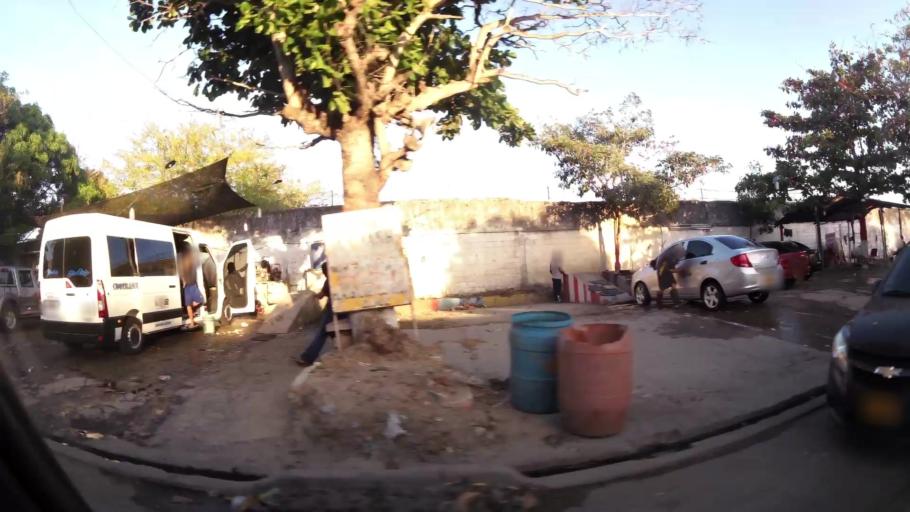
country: CO
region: Atlantico
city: Barranquilla
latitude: 10.9742
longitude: -74.7975
